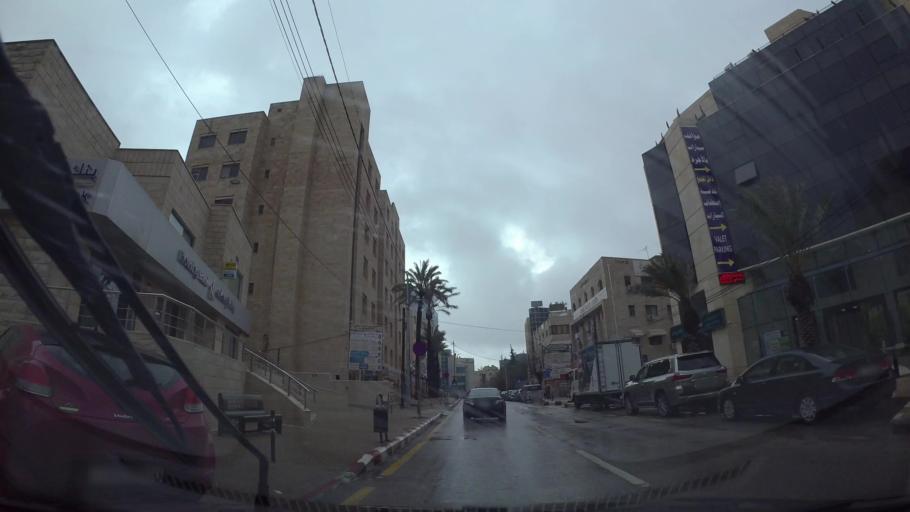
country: JO
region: Amman
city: Amman
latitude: 31.9522
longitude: 35.9014
